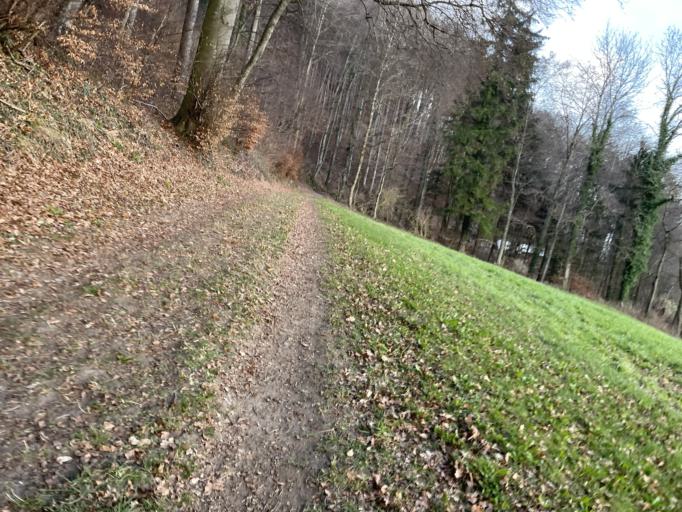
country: CH
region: Bern
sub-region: Bern-Mittelland District
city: Muhlethurnen
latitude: 46.8403
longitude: 7.5265
